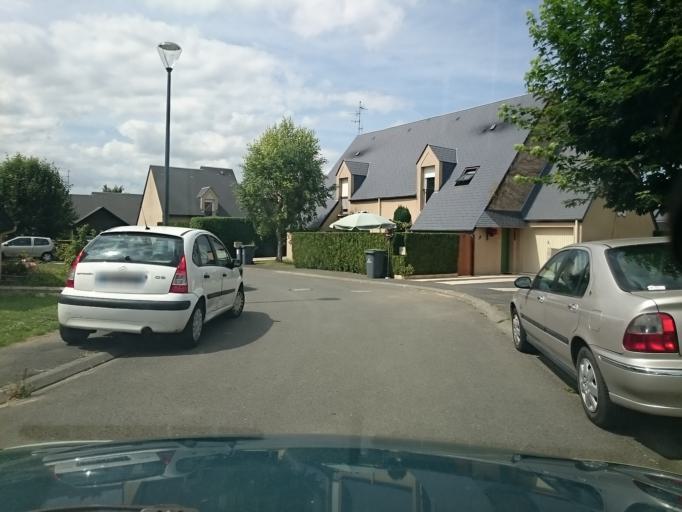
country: FR
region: Lower Normandy
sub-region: Departement du Calvados
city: Ifs
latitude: 49.1371
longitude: -0.3471
